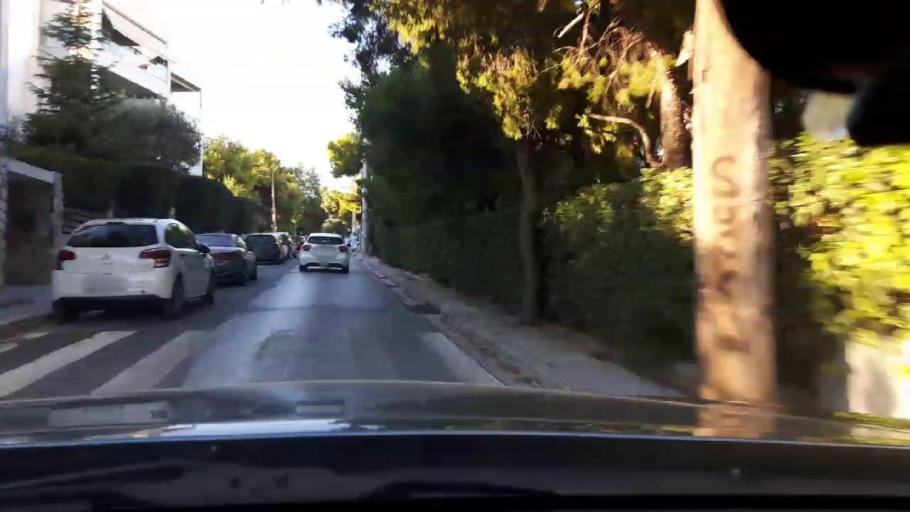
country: GR
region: Attica
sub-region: Nomarchia Athinas
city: Melissia
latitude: 38.0480
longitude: 23.8333
